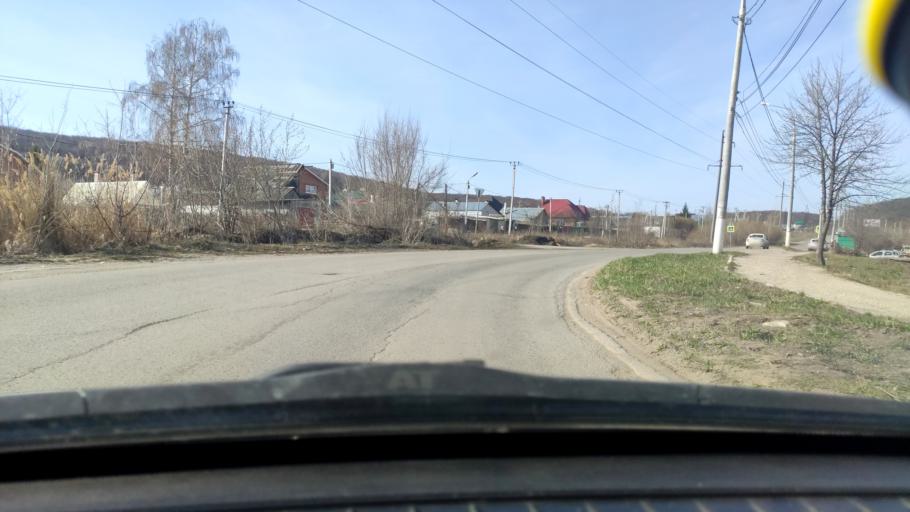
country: RU
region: Samara
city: Zhigulevsk
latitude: 53.3947
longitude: 49.4973
